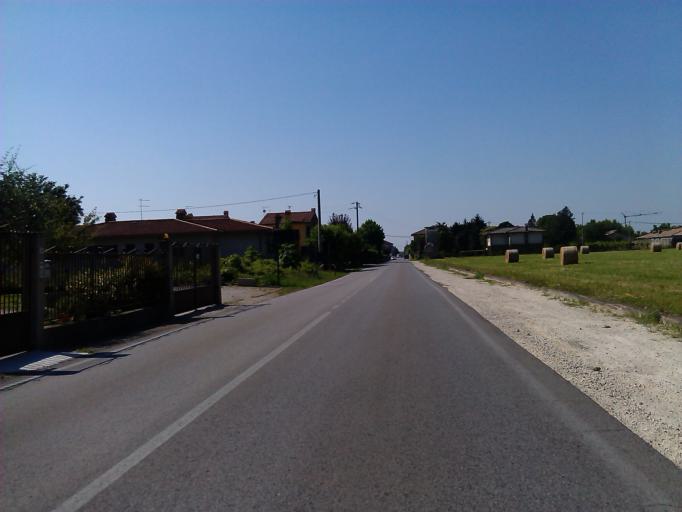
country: IT
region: Veneto
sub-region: Provincia di Vicenza
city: Casoni
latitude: 45.7466
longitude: 11.8113
